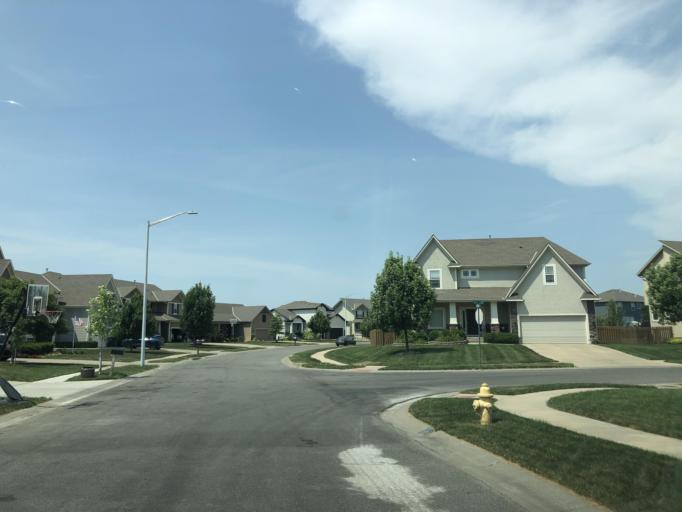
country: US
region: Kansas
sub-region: Johnson County
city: Gardner
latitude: 38.8275
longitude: -94.9612
